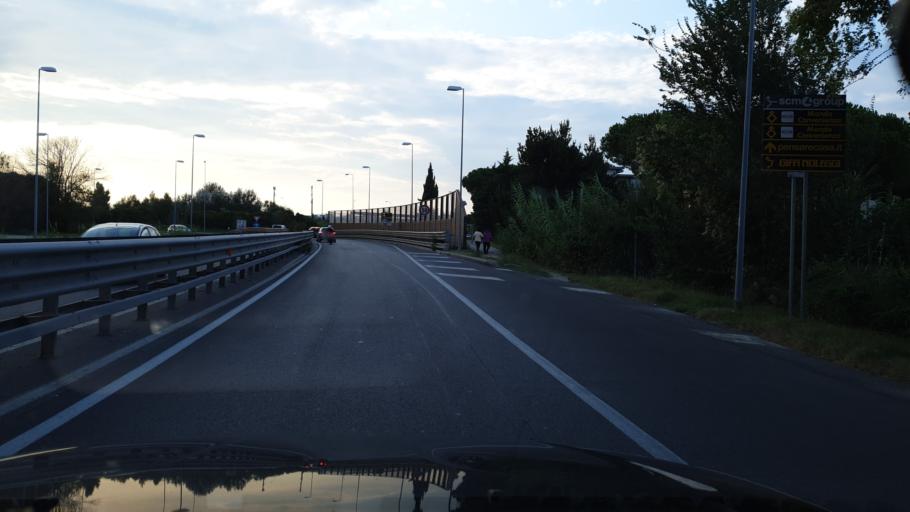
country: IT
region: Emilia-Romagna
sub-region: Provincia di Rimini
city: Rivazzurra
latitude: 44.0400
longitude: 12.5932
